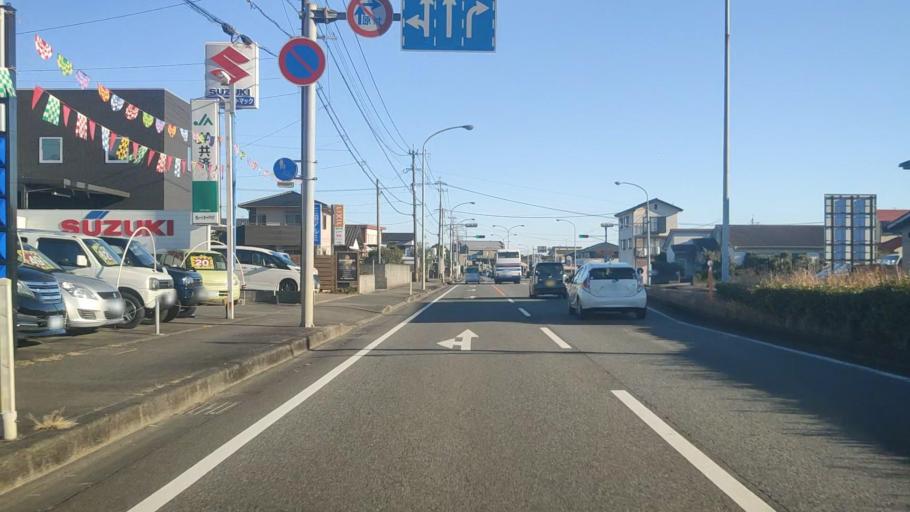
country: JP
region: Miyazaki
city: Nobeoka
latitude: 32.4594
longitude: 131.6466
